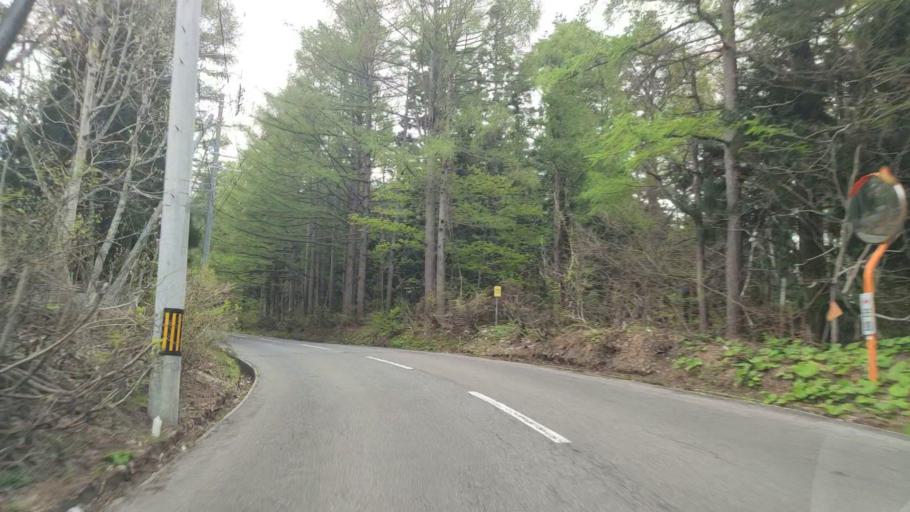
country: JP
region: Aomori
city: Aomori Shi
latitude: 40.7469
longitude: 140.8214
